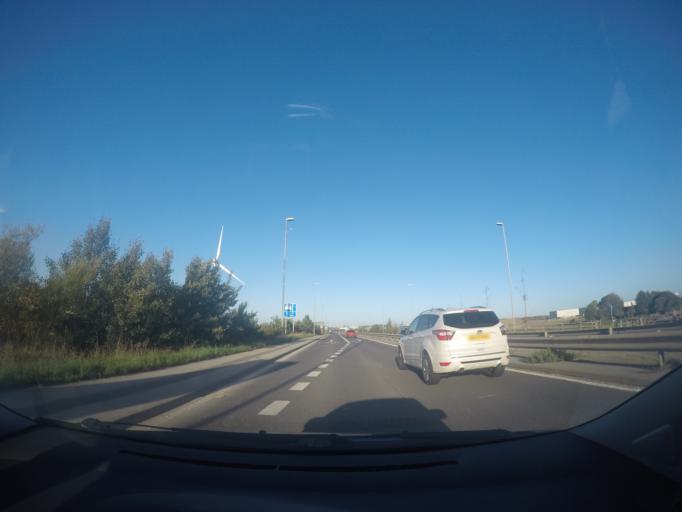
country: GB
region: England
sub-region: City and Borough of Leeds
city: Lofthouse
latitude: 53.7813
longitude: -1.4840
